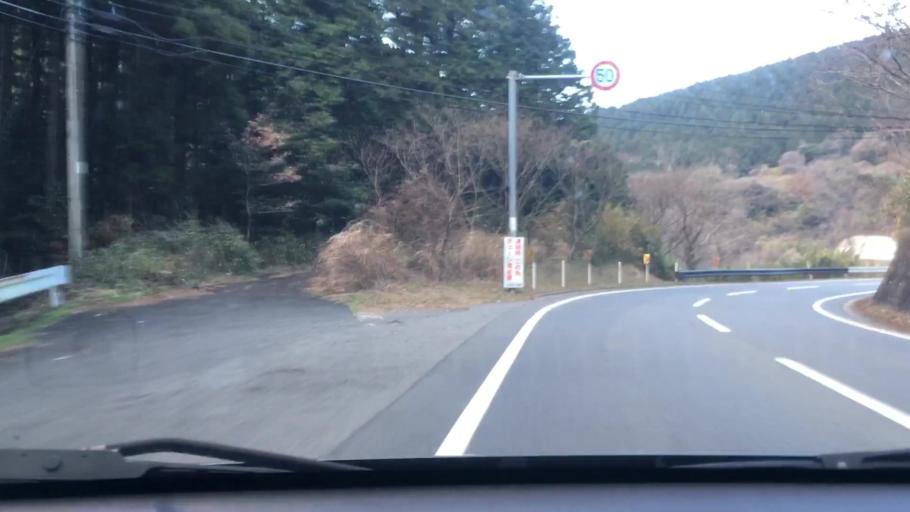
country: JP
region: Oita
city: Hiji
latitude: 33.3672
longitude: 131.4661
